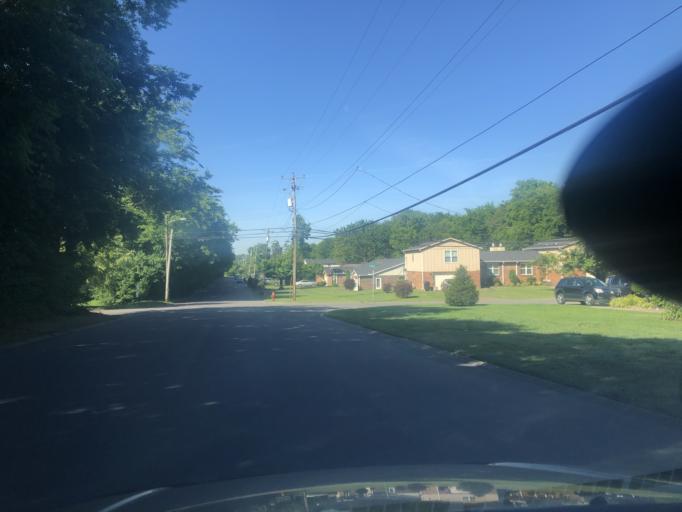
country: US
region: Tennessee
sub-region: Davidson County
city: Lakewood
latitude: 36.2440
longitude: -86.6686
